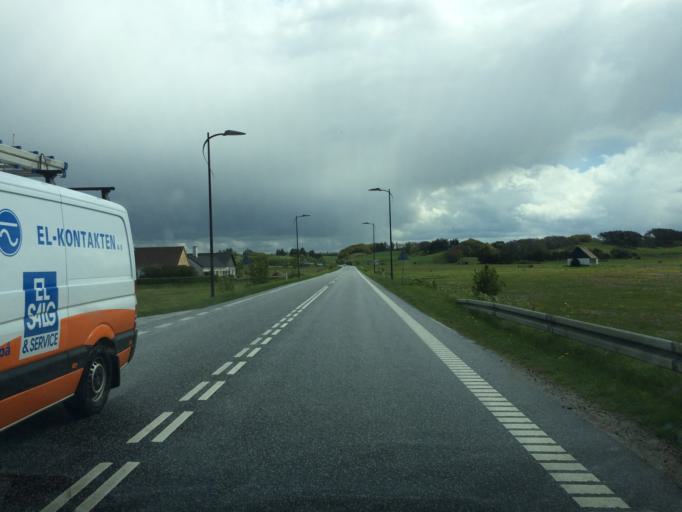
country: DK
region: Central Jutland
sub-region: Skive Kommune
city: Hojslev
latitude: 56.6054
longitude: 9.2945
